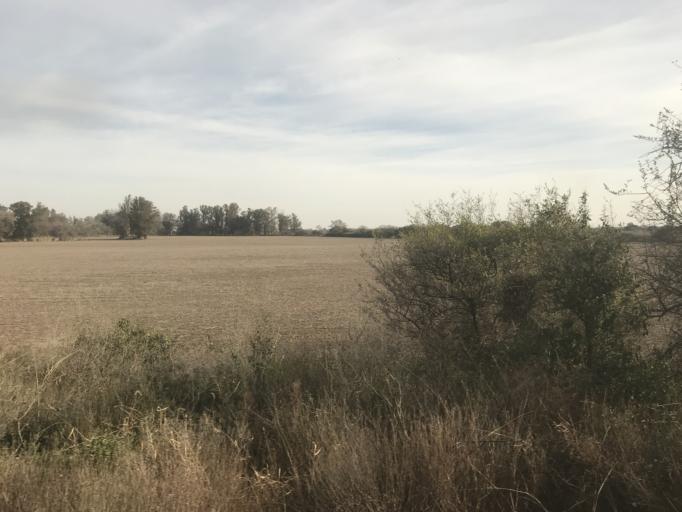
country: AR
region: Cordoba
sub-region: Departamento de Rio Segundo
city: Rio Segundo
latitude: -31.6651
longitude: -63.9005
